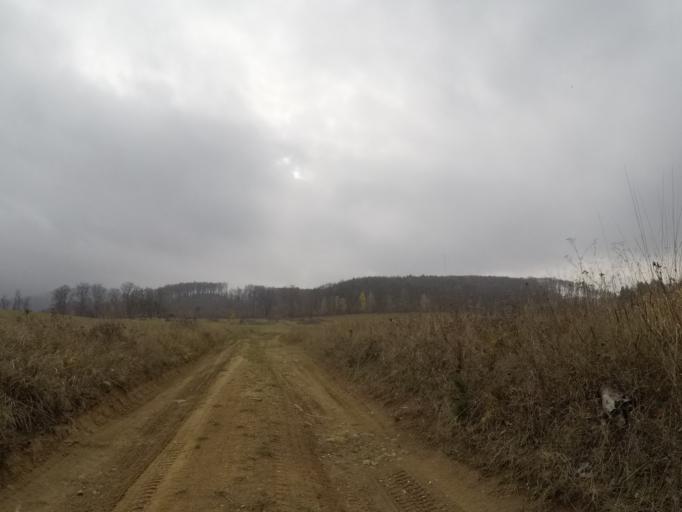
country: SK
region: Presovsky
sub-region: Okres Presov
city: Presov
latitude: 48.8944
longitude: 21.1727
